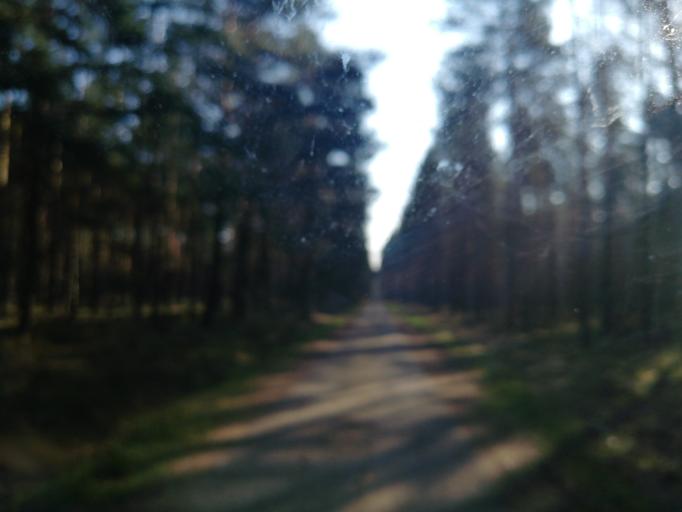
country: DE
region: Brandenburg
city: Drahnsdorf
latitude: 51.8890
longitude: 13.5422
